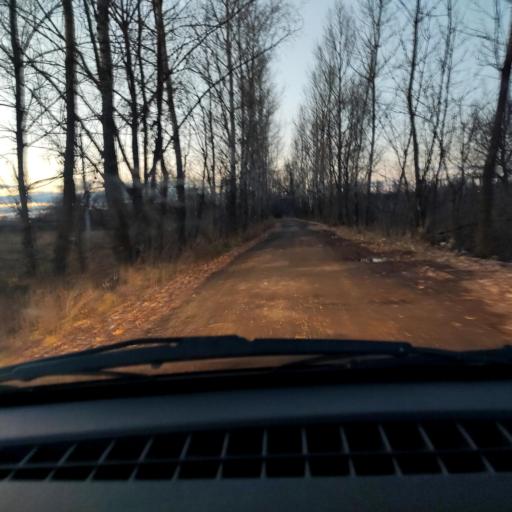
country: RU
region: Bashkortostan
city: Ufa
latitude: 54.6535
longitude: 55.8901
